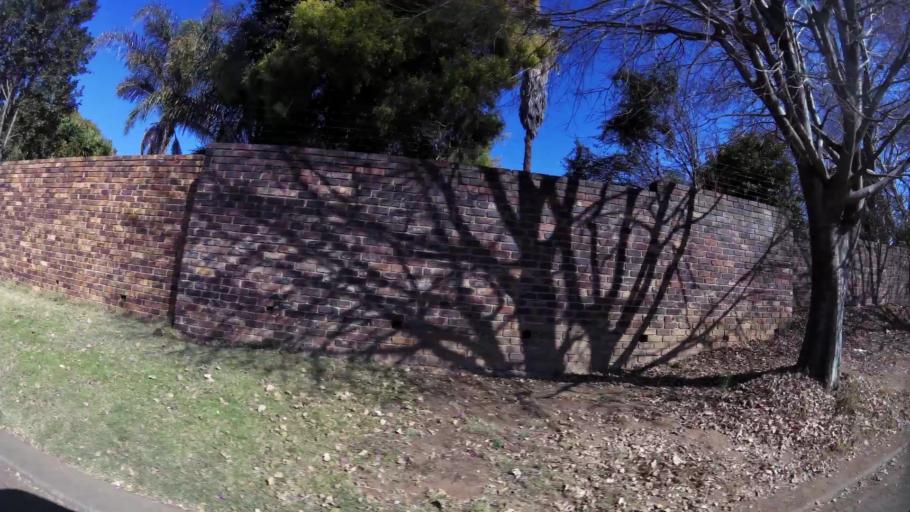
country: ZA
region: Gauteng
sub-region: City of Johannesburg Metropolitan Municipality
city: Modderfontein
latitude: -26.1162
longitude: 28.1091
